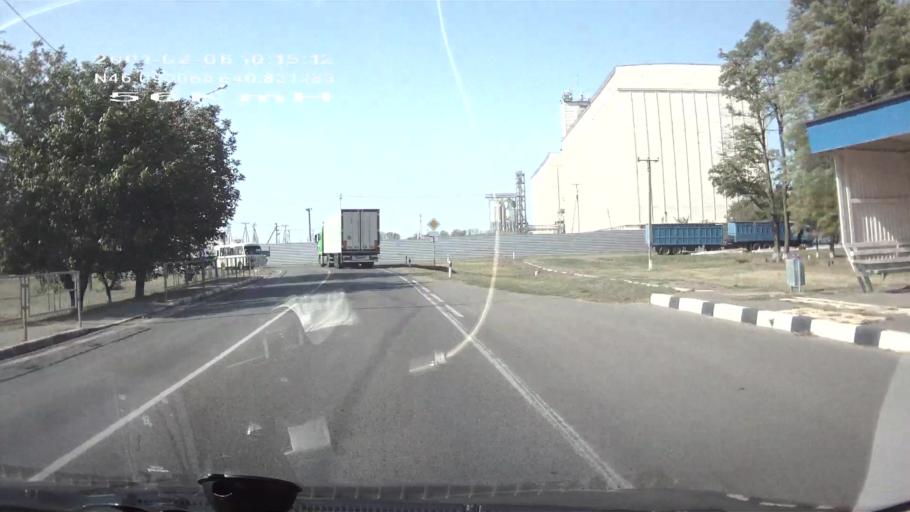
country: RU
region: Krasnodarskiy
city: Belaya Glina
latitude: 46.0900
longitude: 40.8309
